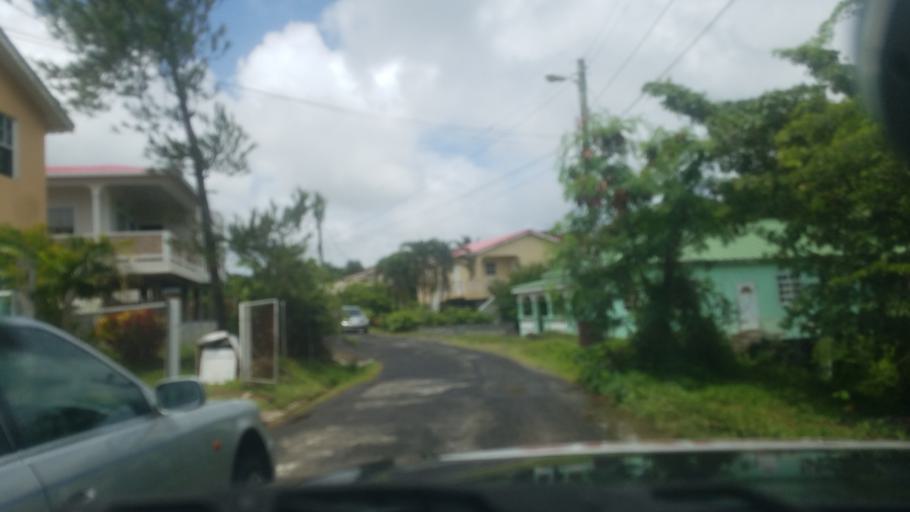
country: LC
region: Laborie Quarter
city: Laborie
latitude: 13.7435
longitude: -60.9726
